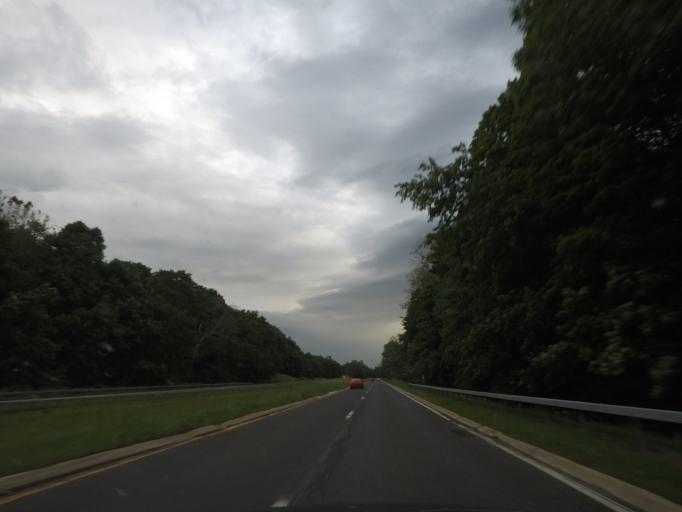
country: US
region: New York
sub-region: Columbia County
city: Philmont
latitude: 42.2319
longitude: -73.6266
